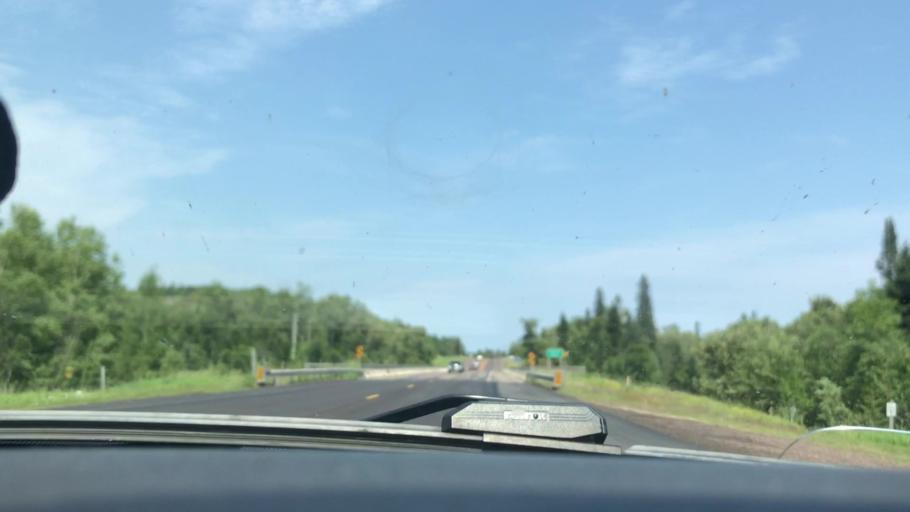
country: US
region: Minnesota
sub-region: Lake County
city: Silver Bay
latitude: 47.3365
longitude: -91.2018
